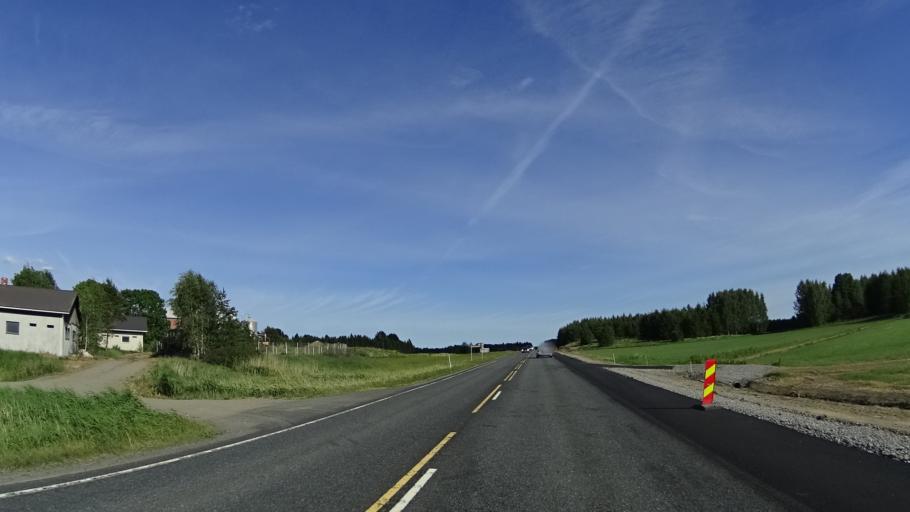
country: FI
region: Haeme
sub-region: Forssa
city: Tammela
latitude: 60.7613
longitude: 23.6948
